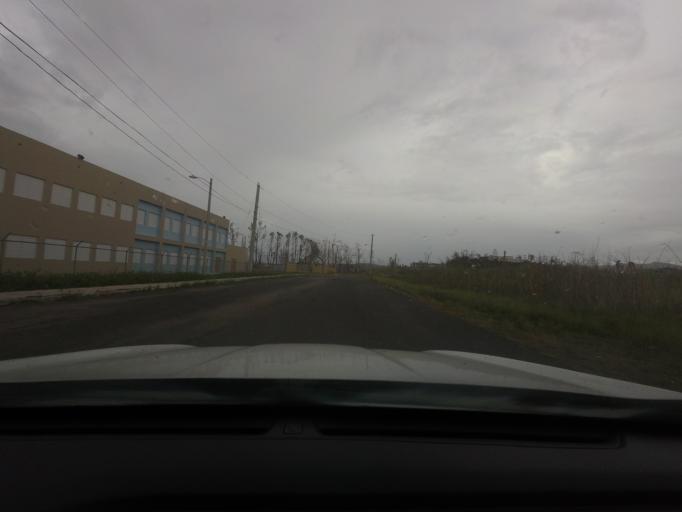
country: PR
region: Ciales
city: Ciales
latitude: 18.2721
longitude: -66.4826
